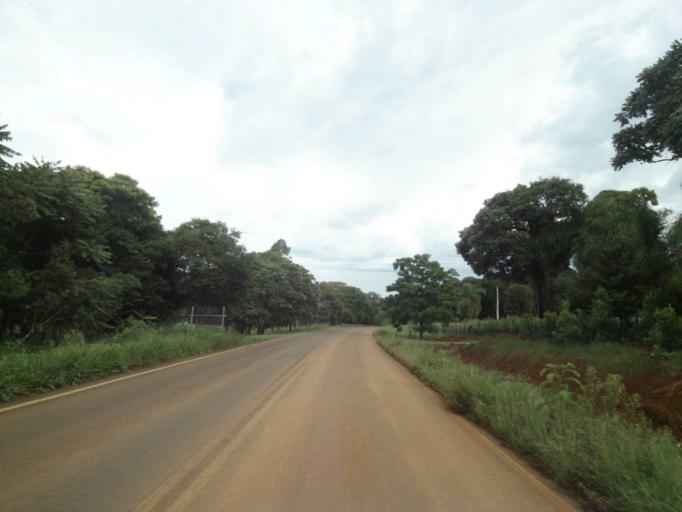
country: BR
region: Parana
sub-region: Pitanga
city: Pitanga
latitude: -24.8954
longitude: -51.9577
